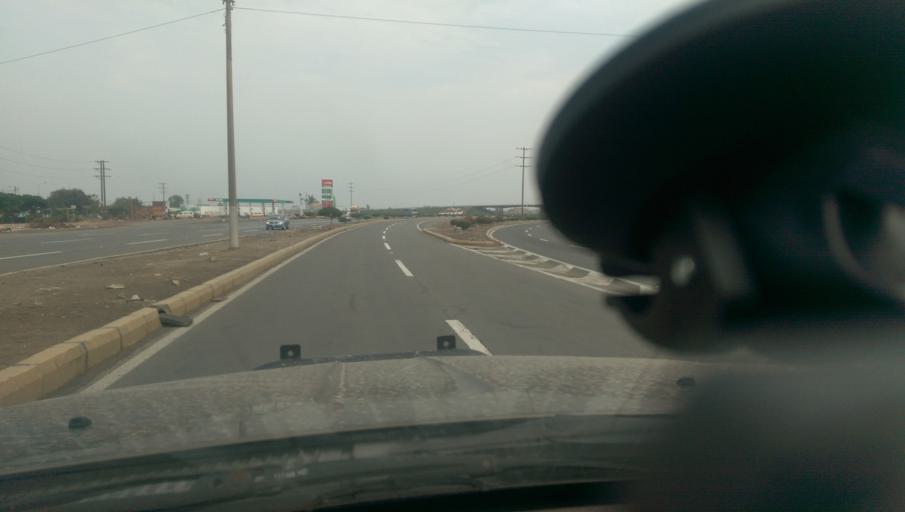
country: PE
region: Lima
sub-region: Lima
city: Santa Rosa
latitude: -11.7802
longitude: -77.1588
